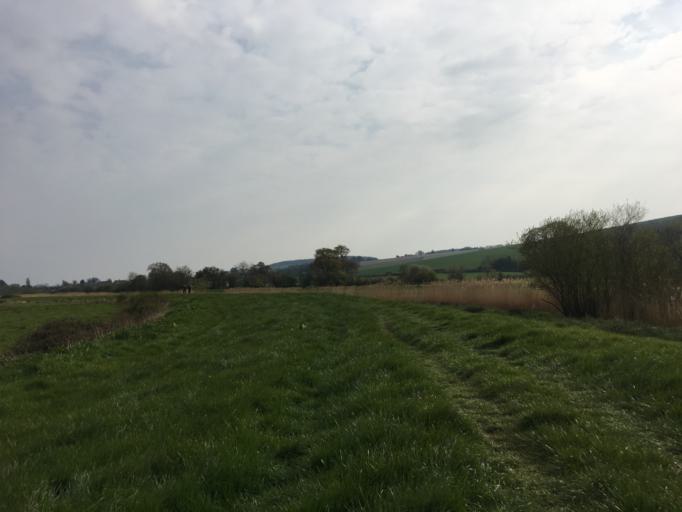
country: GB
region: England
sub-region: West Sussex
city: Arundel
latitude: 50.9050
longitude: -0.5555
